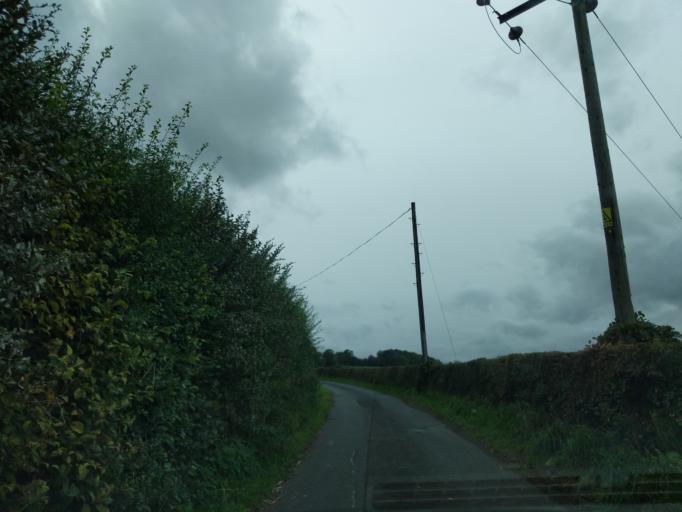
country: GB
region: Scotland
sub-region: The Scottish Borders
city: Melrose
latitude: 55.5991
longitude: -2.7571
